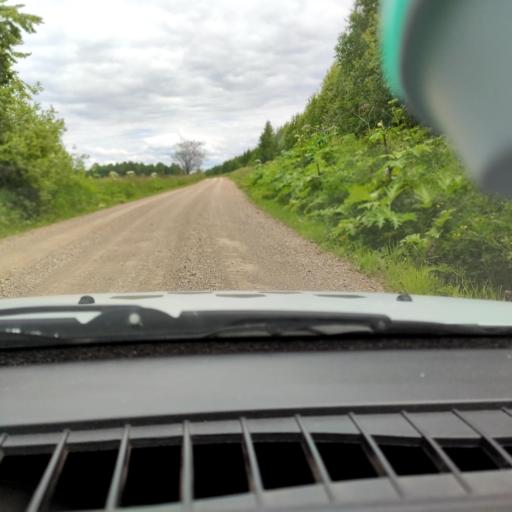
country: RU
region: Perm
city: Suksun
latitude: 57.2115
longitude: 57.6673
